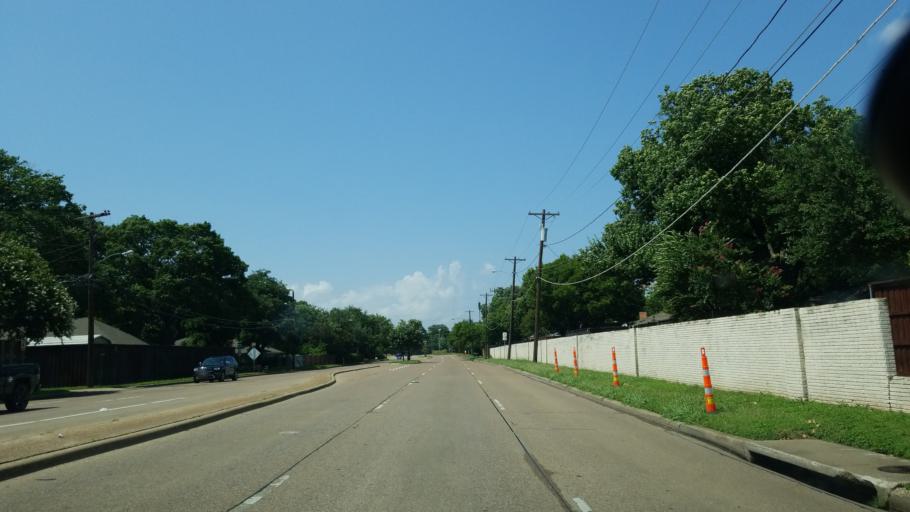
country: US
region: Texas
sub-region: Dallas County
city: Farmers Branch
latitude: 32.8823
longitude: -96.8657
